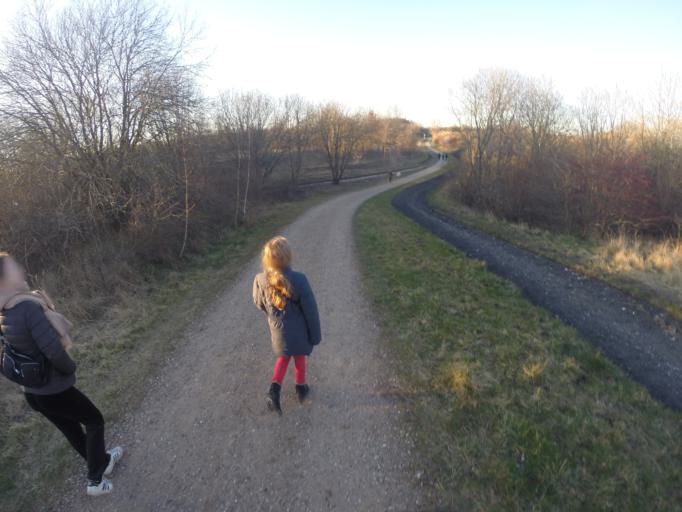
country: DK
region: Capital Region
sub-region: Hoje-Taastrup Kommune
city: Flong
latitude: 55.6369
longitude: 12.1872
